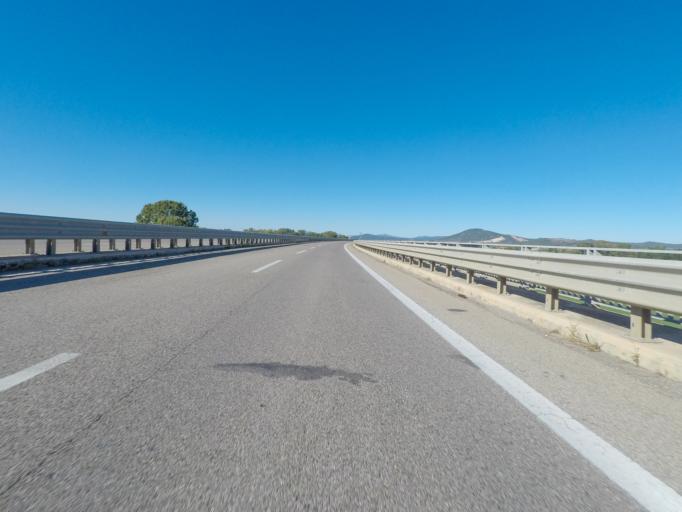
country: IT
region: Tuscany
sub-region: Provincia di Grosseto
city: Grosseto
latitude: 42.7621
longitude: 11.1421
